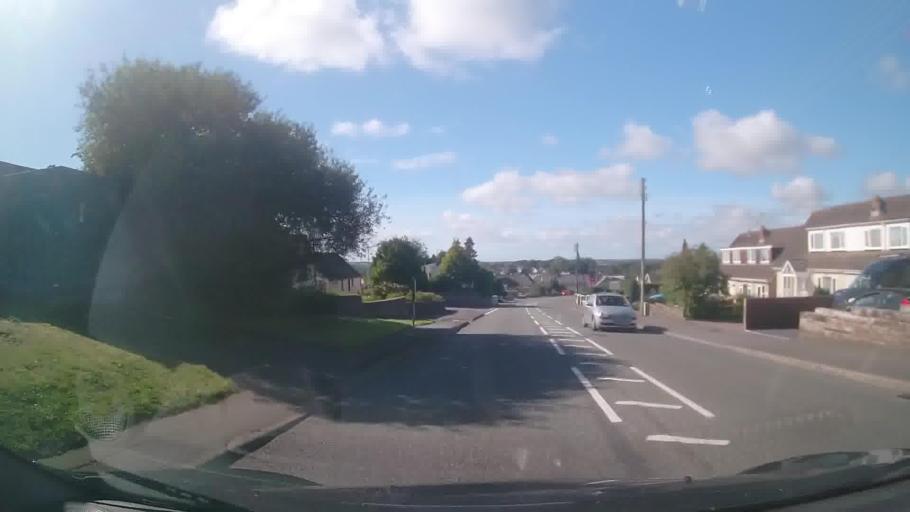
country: GB
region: Wales
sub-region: Pembrokeshire
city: Kilgetty
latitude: 51.7203
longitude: -4.7289
